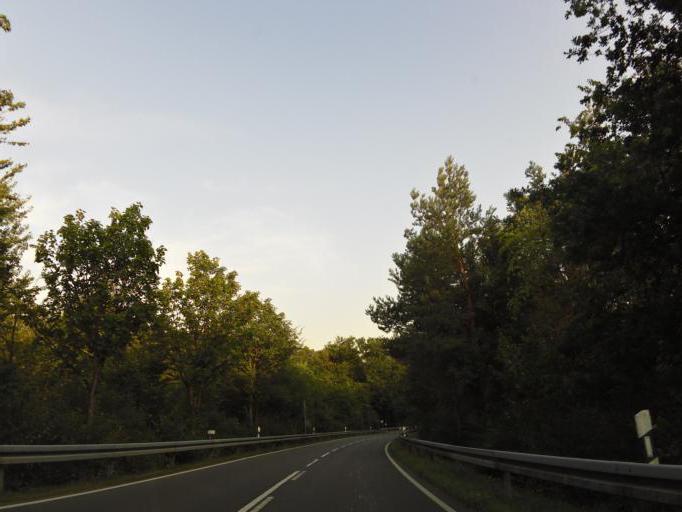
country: DE
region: Hesse
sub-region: Regierungsbezirk Darmstadt
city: Buttelborn
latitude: 49.9538
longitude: 8.5399
